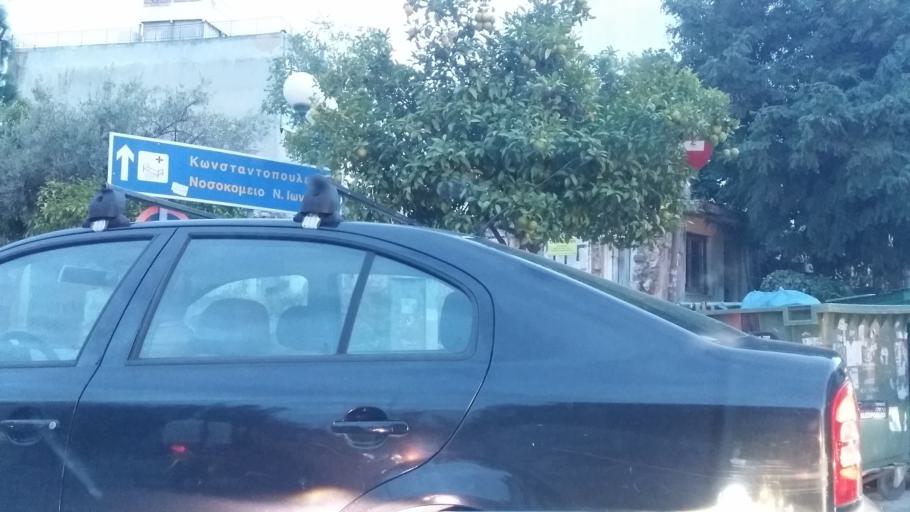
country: GR
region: Attica
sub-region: Nomarchia Athinas
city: Nea Ionia
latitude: 38.0407
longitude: 23.7506
